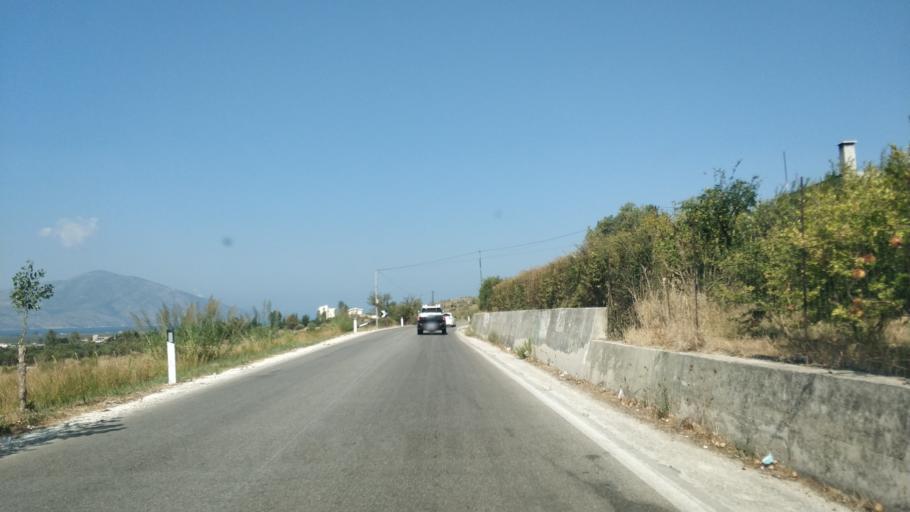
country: AL
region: Vlore
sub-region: Rrethi i Vlores
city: Orikum
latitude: 40.3094
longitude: 19.4807
